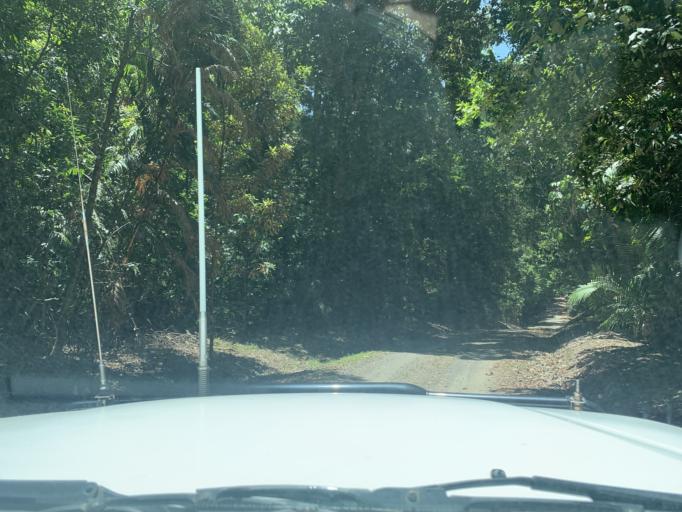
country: AU
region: Queensland
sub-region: Cairns
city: Redlynch
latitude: -16.9637
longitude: 145.6457
